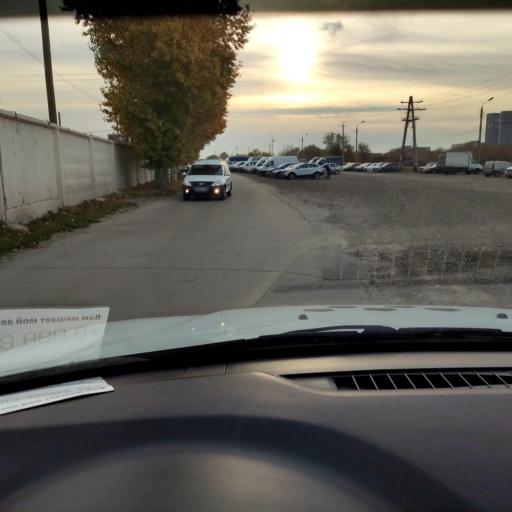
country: RU
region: Samara
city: Tol'yatti
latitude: 53.5700
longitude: 49.4631
